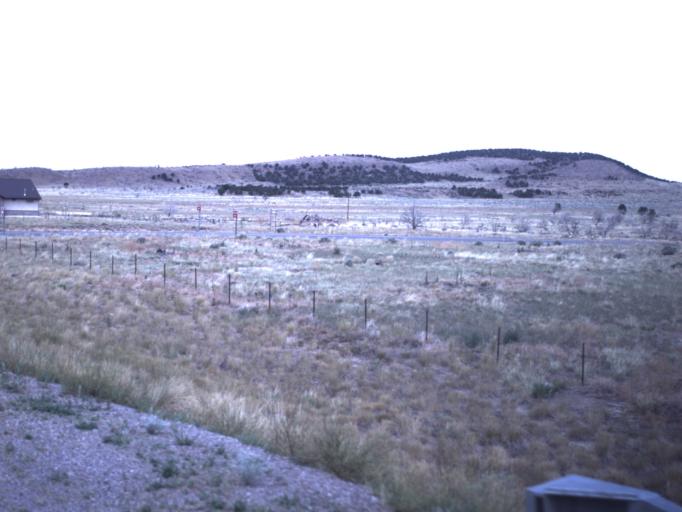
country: US
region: Utah
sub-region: Beaver County
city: Beaver
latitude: 38.6159
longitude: -112.6107
